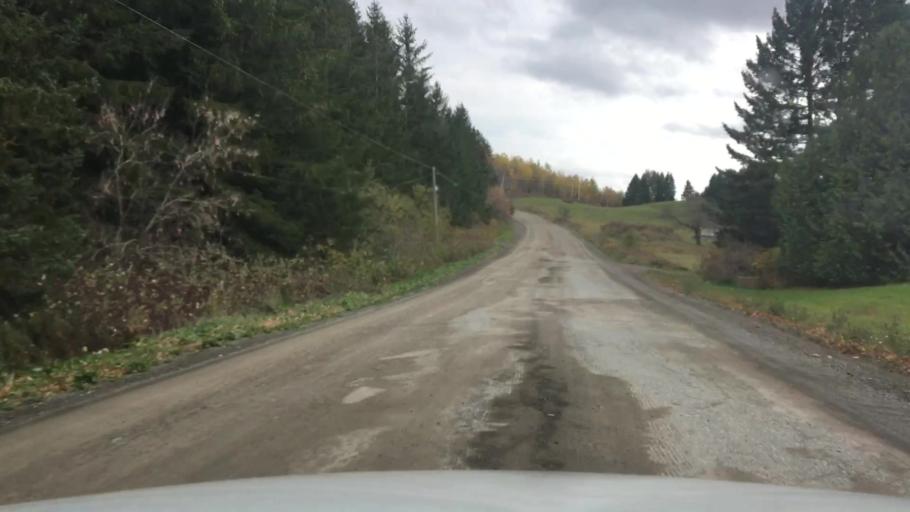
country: US
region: Maine
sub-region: Aroostook County
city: Easton
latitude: 46.5200
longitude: -67.8870
